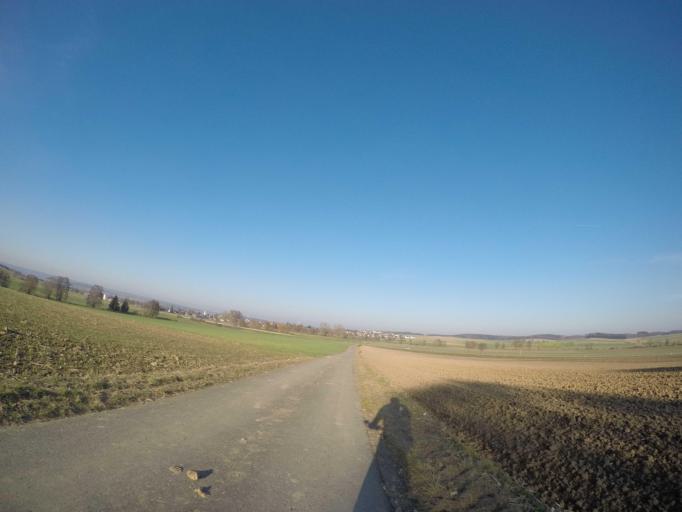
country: DE
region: Baden-Wuerttemberg
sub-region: Tuebingen Region
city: Oberstadion
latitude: 48.1929
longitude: 9.6866
